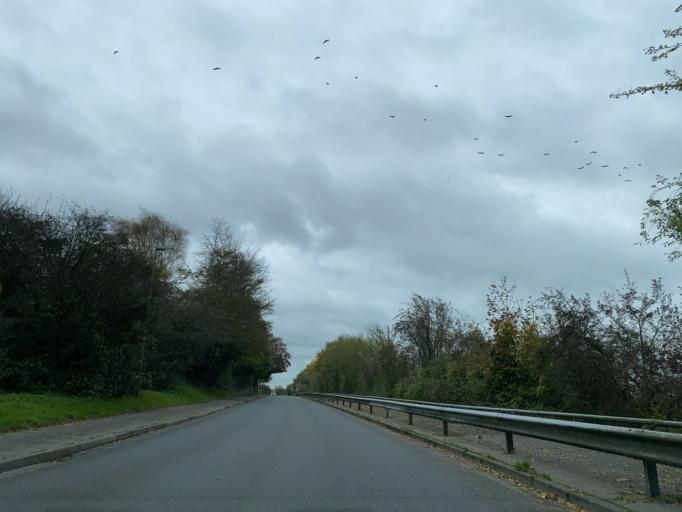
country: DE
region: Schleswig-Holstein
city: Flensburg
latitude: 54.7723
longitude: 9.4467
